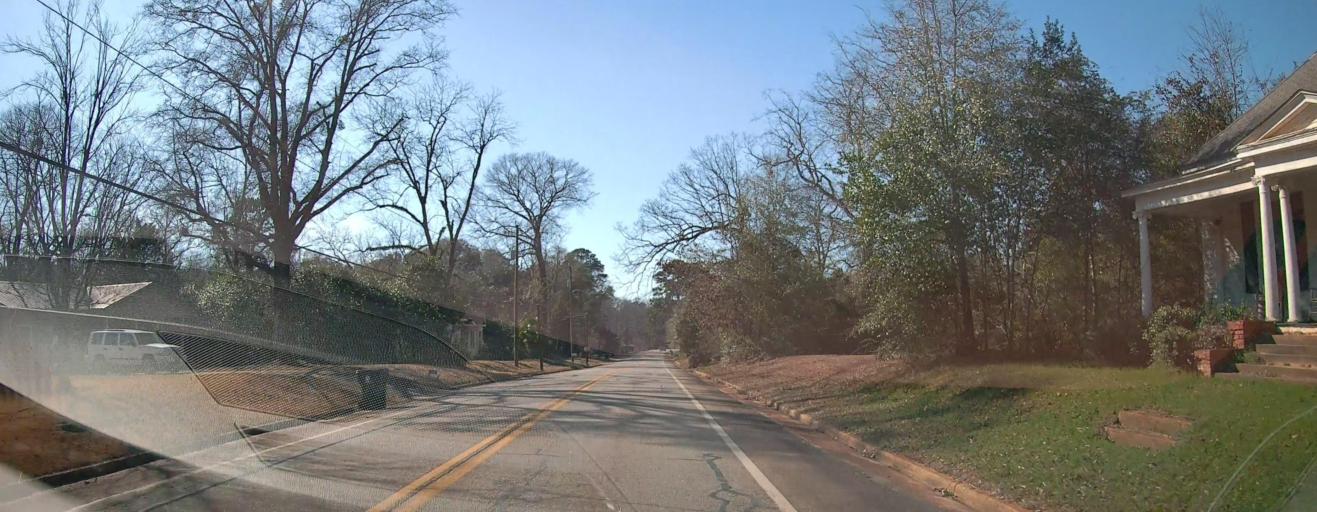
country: US
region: Georgia
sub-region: Macon County
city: Oglethorpe
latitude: 32.1962
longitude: -84.1426
